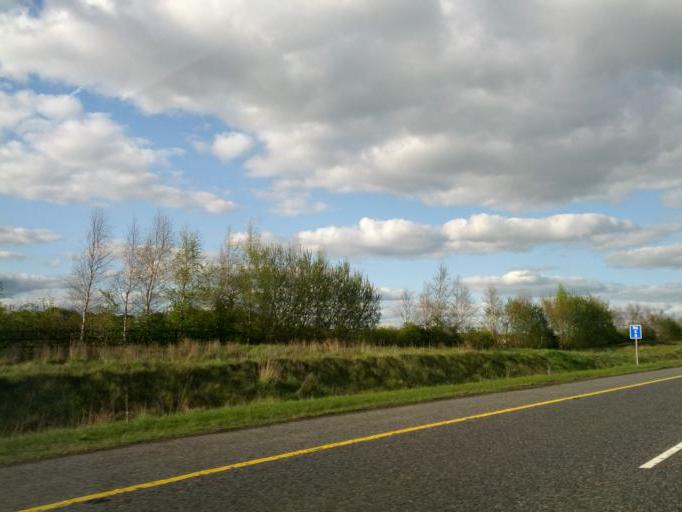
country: IE
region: Leinster
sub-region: An Iarmhi
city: Rochfortbridge
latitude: 53.4392
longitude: -7.2102
